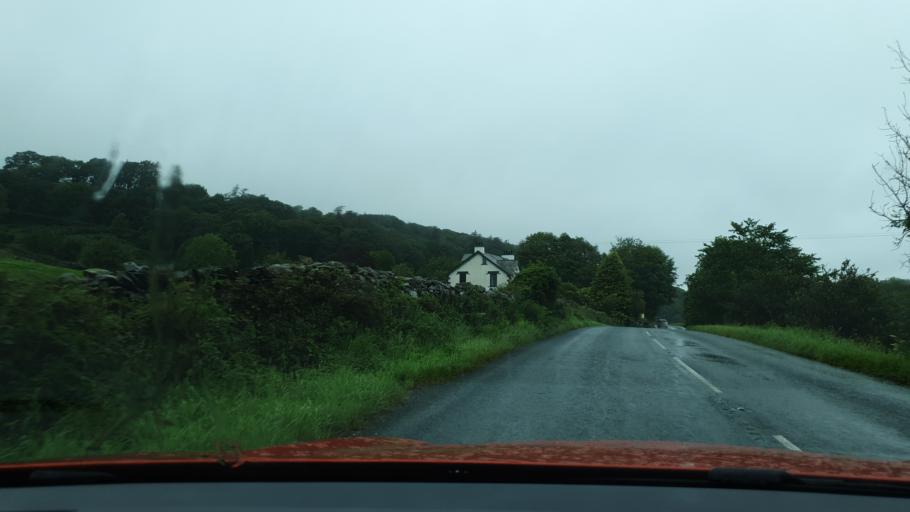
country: GB
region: England
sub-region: Cumbria
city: Ulverston
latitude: 54.3438
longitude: -3.0943
